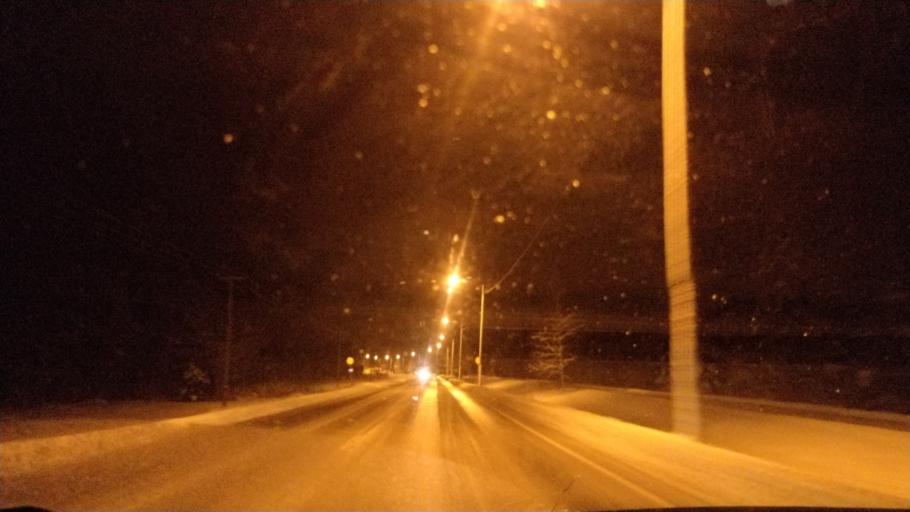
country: FI
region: Lapland
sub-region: Rovaniemi
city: Rovaniemi
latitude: 66.3041
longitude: 25.3563
